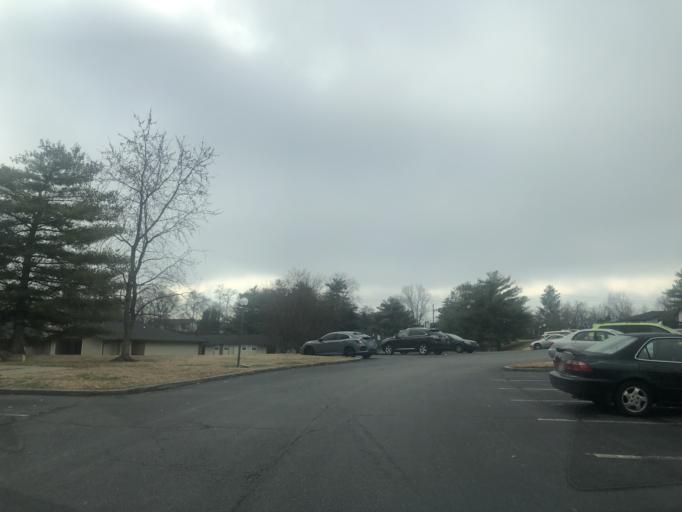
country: US
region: Tennessee
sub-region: Rutherford County
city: La Vergne
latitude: 36.0690
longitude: -86.6420
